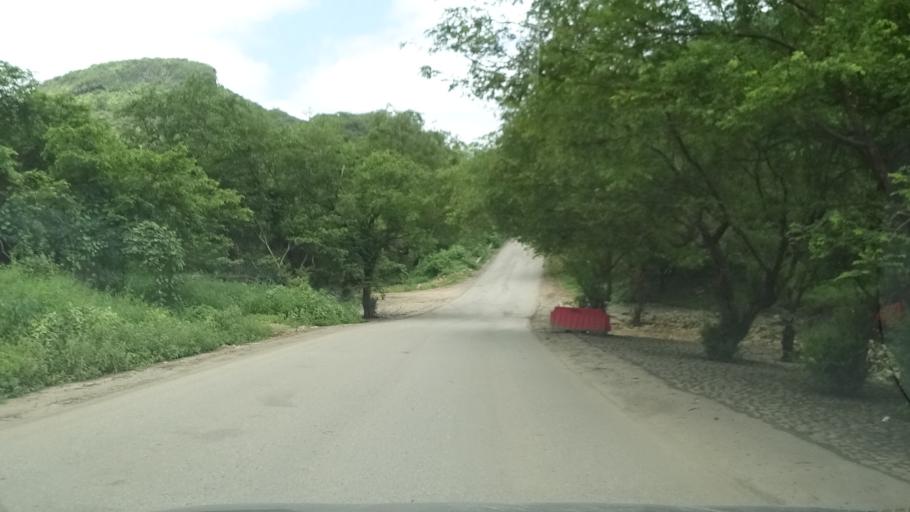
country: OM
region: Zufar
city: Salalah
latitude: 17.1598
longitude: 54.1691
